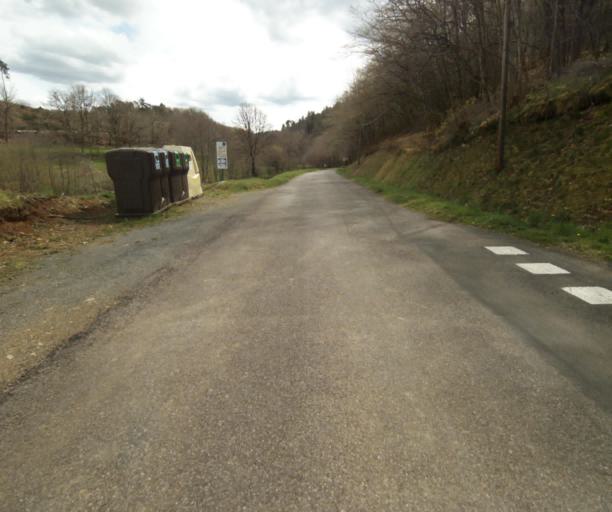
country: FR
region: Limousin
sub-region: Departement de la Correze
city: Laguenne
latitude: 45.2311
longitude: 1.8535
